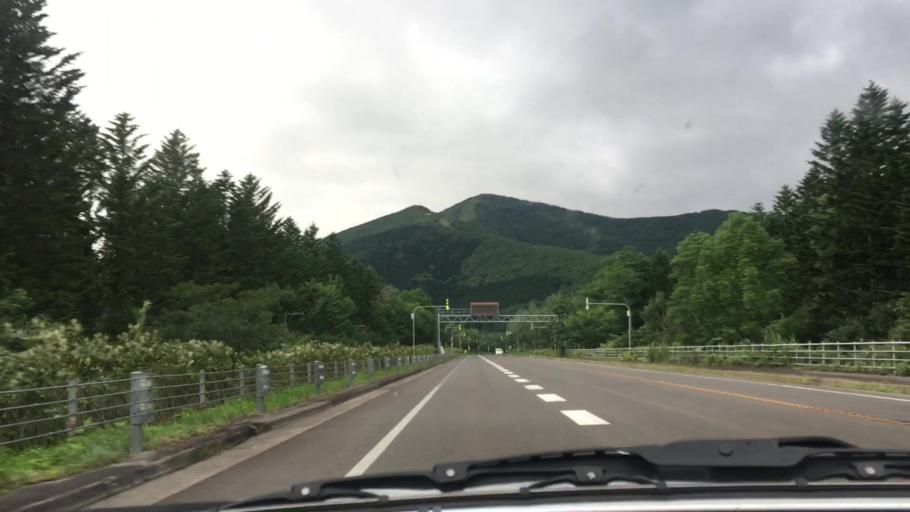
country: JP
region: Hokkaido
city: Otofuke
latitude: 43.1614
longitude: 142.8153
